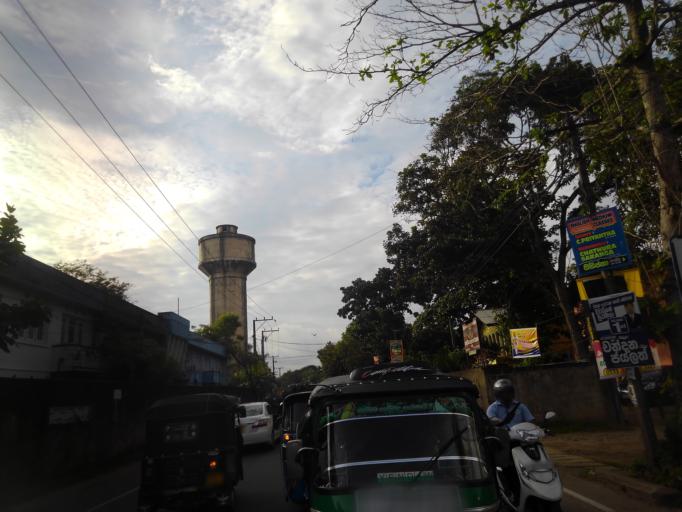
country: LK
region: Southern
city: Galle
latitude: 6.0368
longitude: 80.2296
